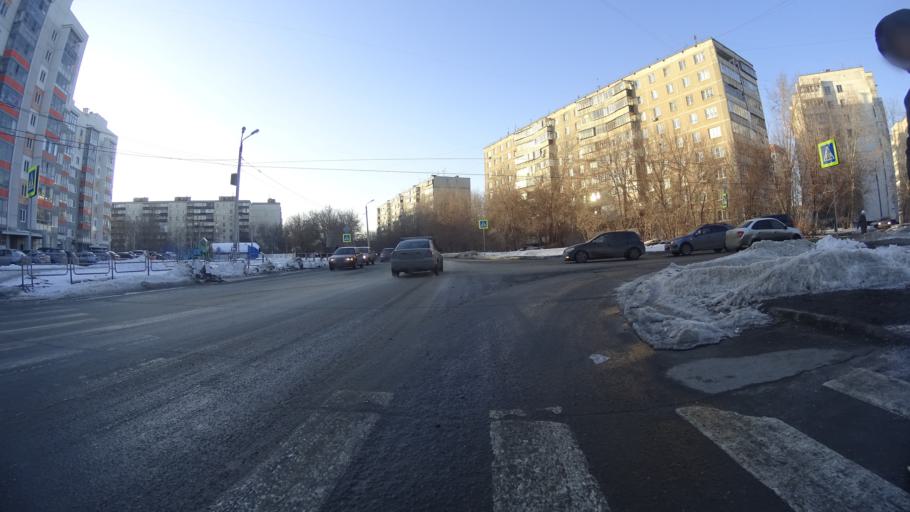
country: RU
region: Chelyabinsk
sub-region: Gorod Chelyabinsk
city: Chelyabinsk
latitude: 55.1375
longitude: 61.4479
